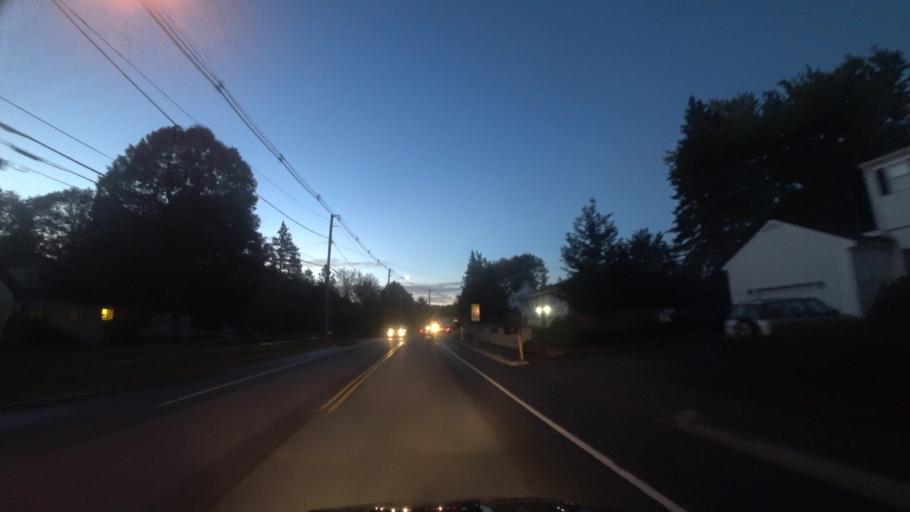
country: US
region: Massachusetts
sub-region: Middlesex County
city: Reading
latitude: 42.5431
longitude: -71.0893
